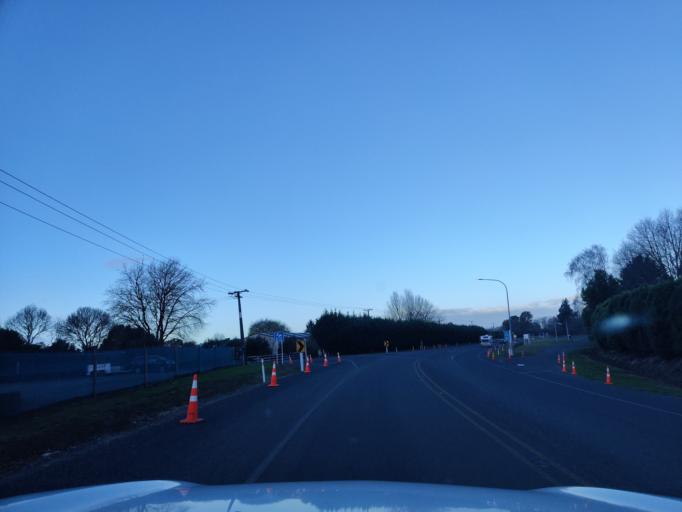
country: NZ
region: Waikato
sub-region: Waipa District
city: Cambridge
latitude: -37.8883
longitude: 175.4381
